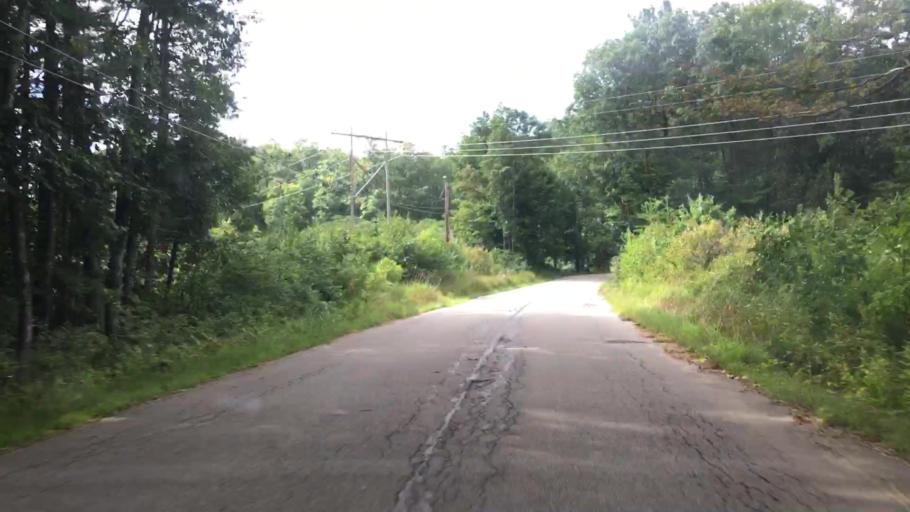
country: US
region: New Hampshire
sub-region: Strafford County
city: Madbury
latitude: 43.1611
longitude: -70.9231
